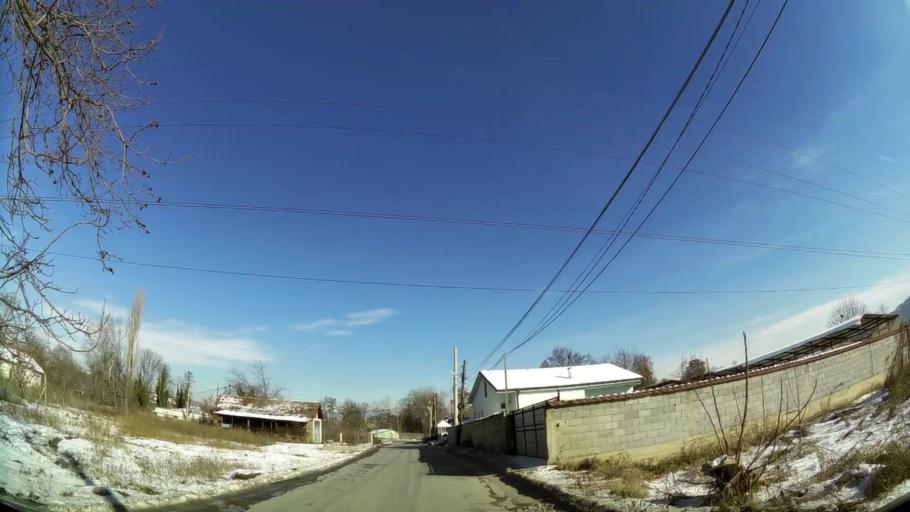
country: MK
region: Saraj
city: Saraj
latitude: 41.9940
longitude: 21.3268
